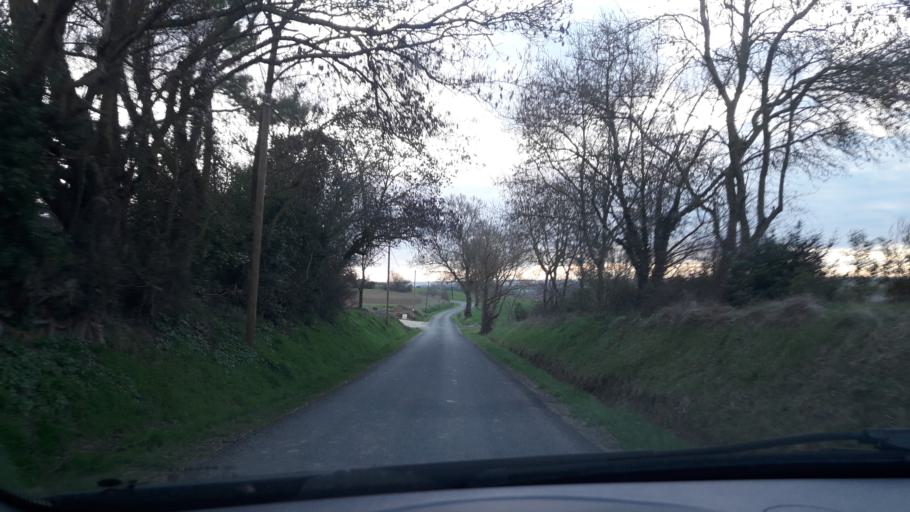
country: FR
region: Midi-Pyrenees
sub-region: Departement du Gers
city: Pujaudran
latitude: 43.6697
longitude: 1.0295
